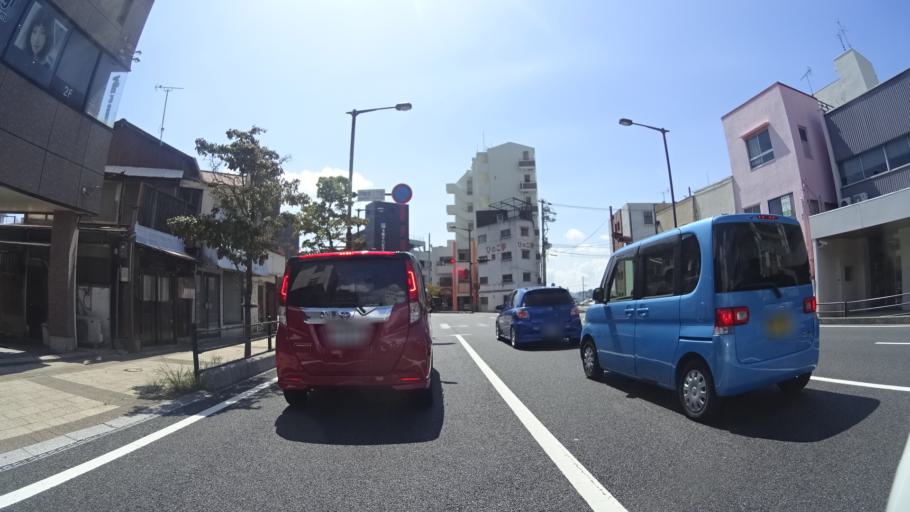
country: JP
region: Yamaguchi
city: Shimonoseki
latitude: 33.9542
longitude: 130.9202
